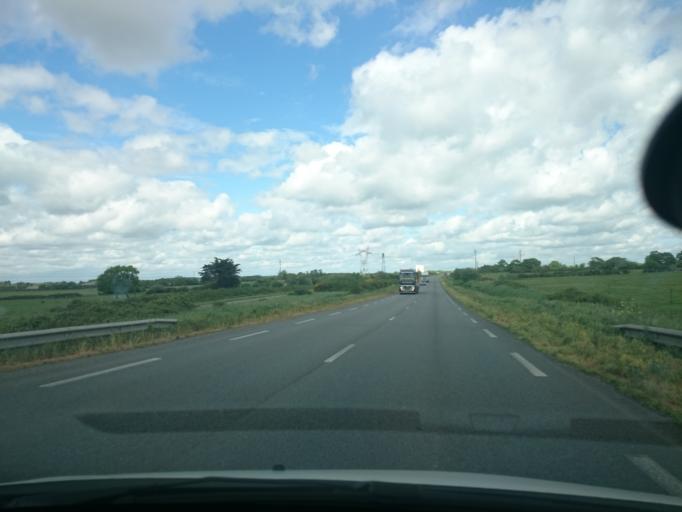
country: FR
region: Pays de la Loire
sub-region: Departement de la Loire-Atlantique
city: Donges
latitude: 47.3259
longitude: -2.1083
